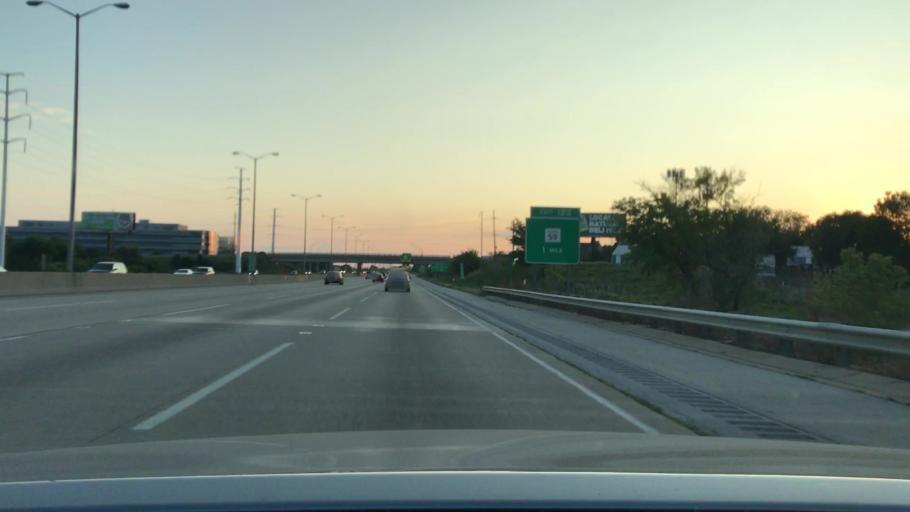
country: US
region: Illinois
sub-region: DuPage County
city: Warrenville
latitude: 41.8055
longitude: -88.1845
